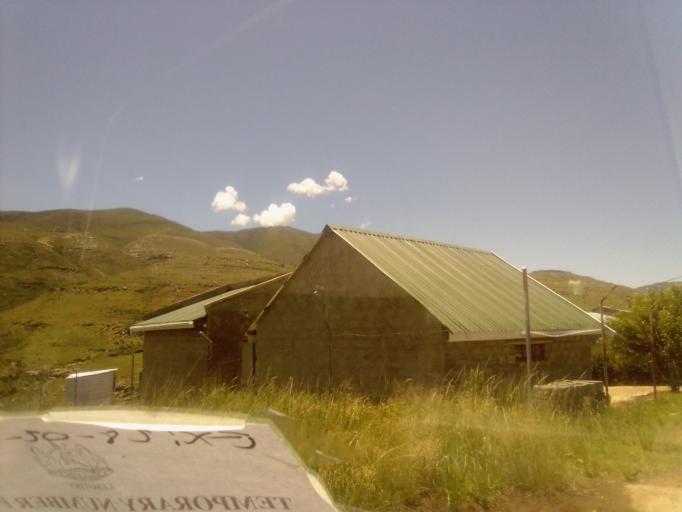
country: LS
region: Qacha's Nek
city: Qacha's Nek
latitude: -30.0903
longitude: 28.6432
